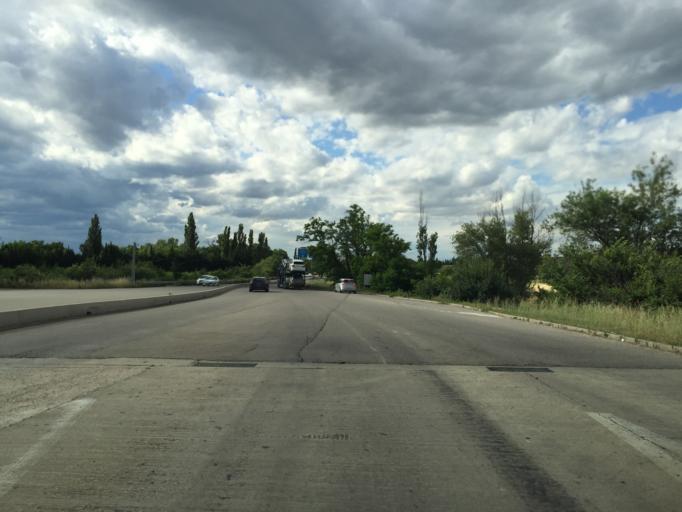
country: FR
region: Provence-Alpes-Cote d'Azur
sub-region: Departement des Bouches-du-Rhone
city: Noves
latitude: 43.8931
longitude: 4.9159
